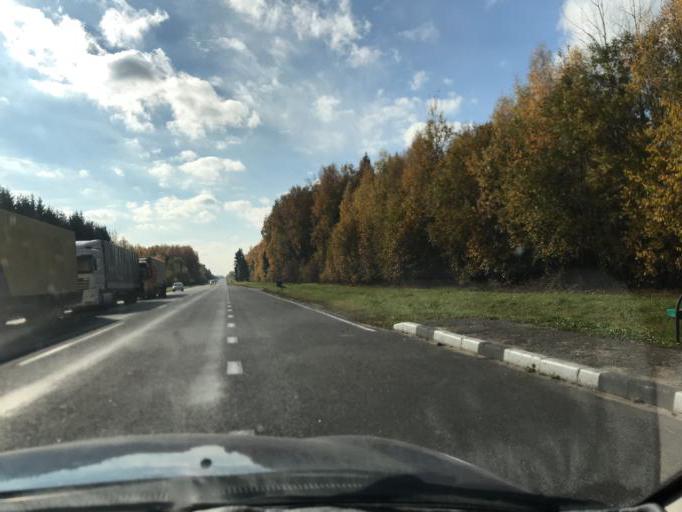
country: LT
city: Salcininkai
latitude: 54.2211
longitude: 25.3553
